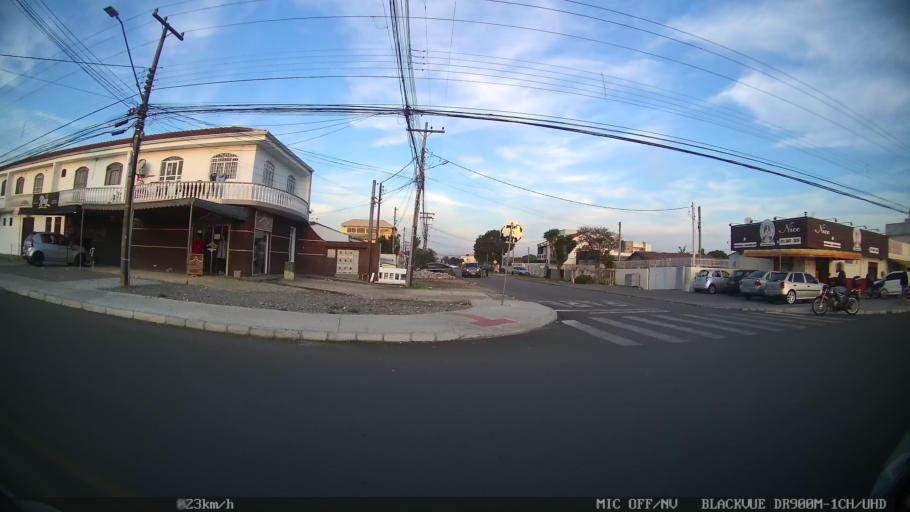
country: BR
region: Parana
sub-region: Pinhais
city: Pinhais
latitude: -25.4612
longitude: -49.1856
